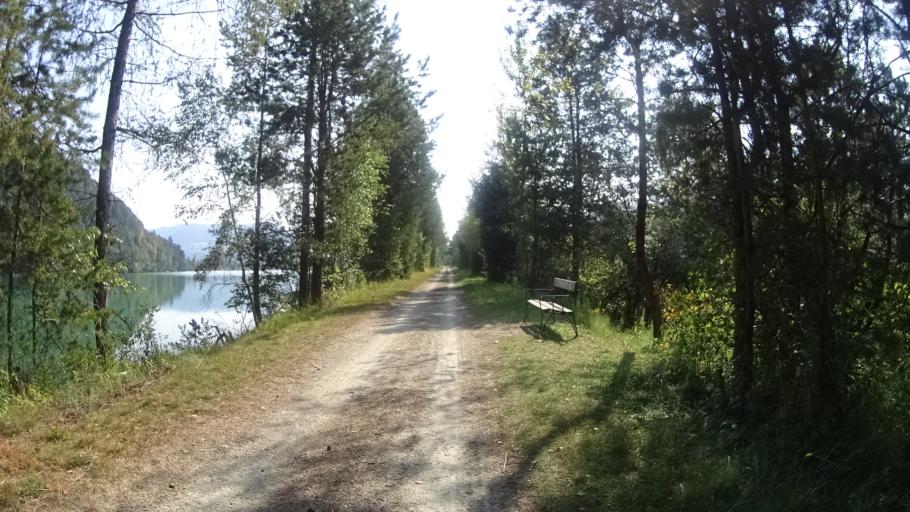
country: AT
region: Carinthia
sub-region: Politischer Bezirk Klagenfurt Land
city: Ebenthal
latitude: 46.5538
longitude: 14.3980
